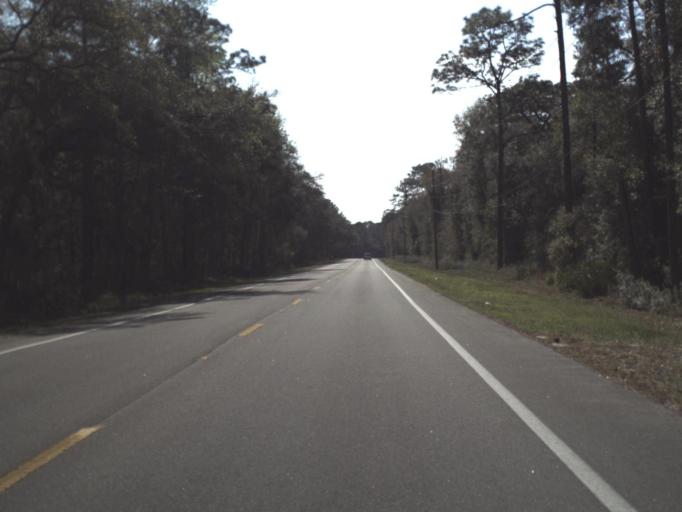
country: US
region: Florida
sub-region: Wakulla County
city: Crawfordville
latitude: 30.0788
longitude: -84.4000
